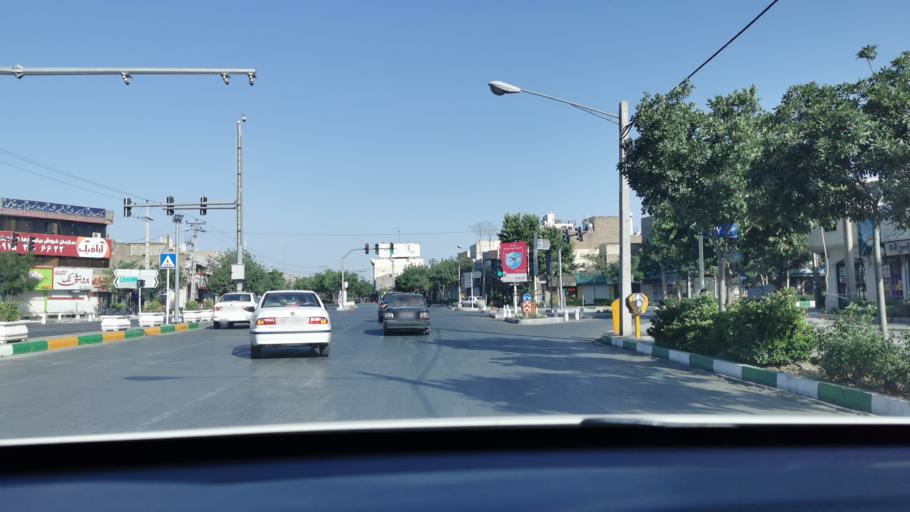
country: IR
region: Razavi Khorasan
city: Mashhad
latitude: 36.3335
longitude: 59.5126
